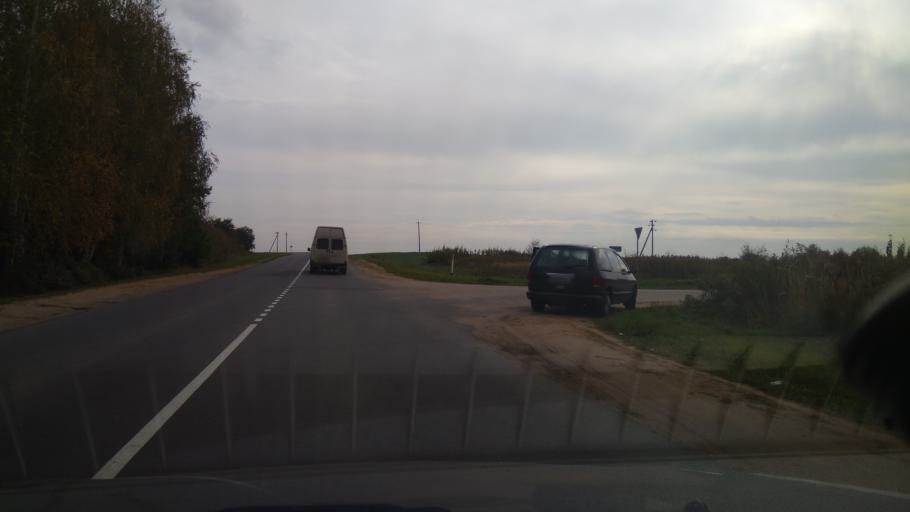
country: BY
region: Minsk
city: Rudzyensk
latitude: 53.6110
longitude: 27.7985
